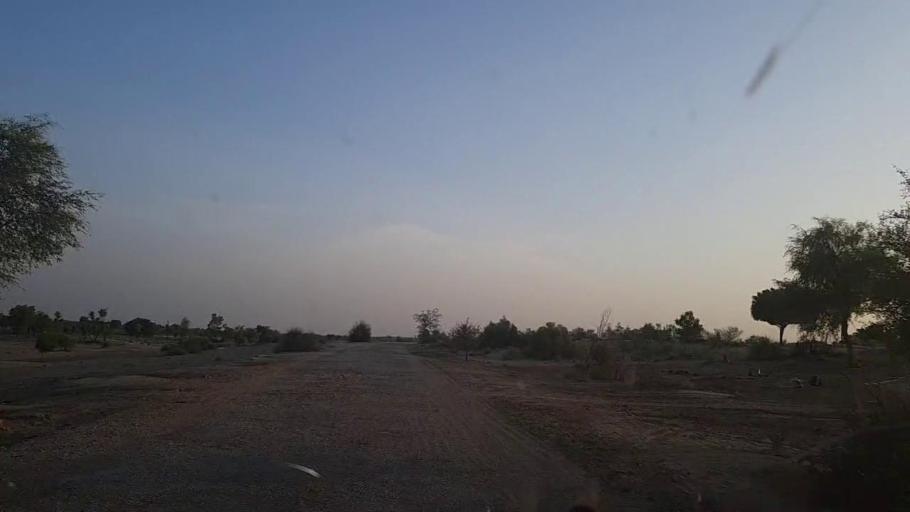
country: PK
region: Sindh
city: Khanpur
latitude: 27.5958
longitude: 69.4258
